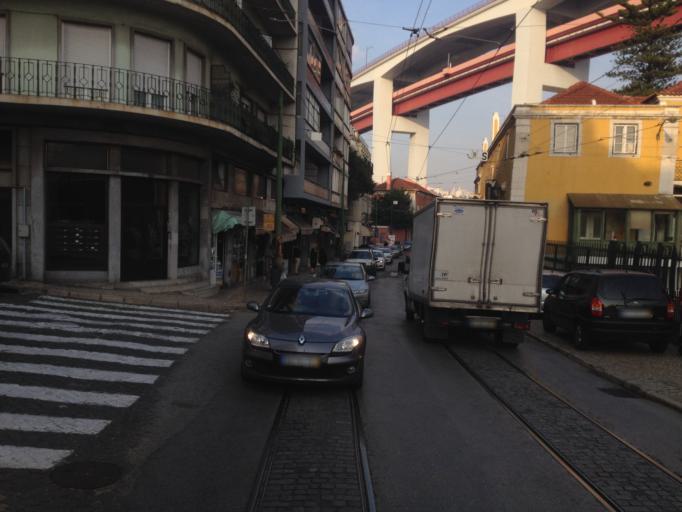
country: PT
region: Setubal
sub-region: Almada
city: Pragal
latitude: 38.7019
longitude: -9.1810
